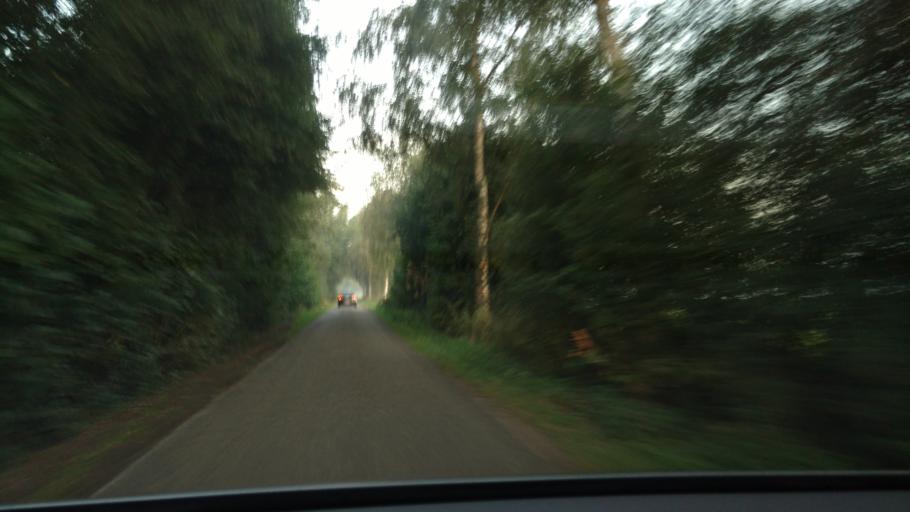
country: DE
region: North Rhine-Westphalia
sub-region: Regierungsbezirk Munster
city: Velen
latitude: 51.8570
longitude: 7.0222
